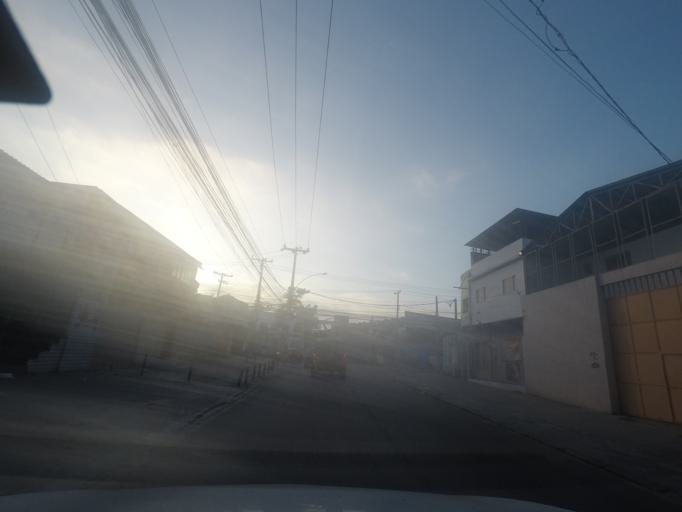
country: BR
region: Rio de Janeiro
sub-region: Duque De Caxias
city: Duque de Caxias
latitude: -22.8362
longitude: -43.2808
